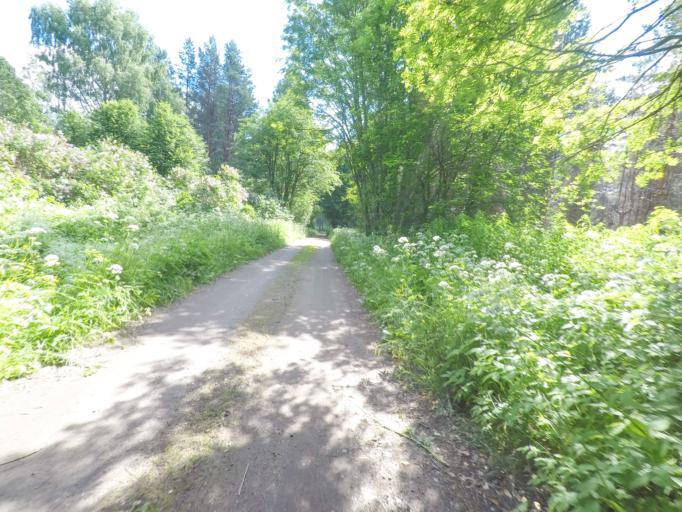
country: FI
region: Southern Savonia
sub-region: Savonlinna
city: Punkaharju
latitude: 61.8067
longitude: 29.3212
